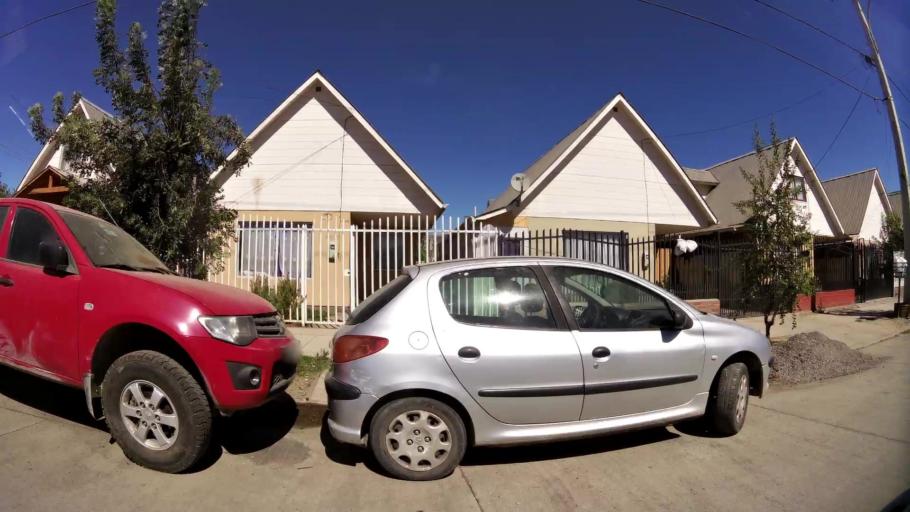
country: CL
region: O'Higgins
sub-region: Provincia de Cachapoal
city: Rancagua
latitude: -34.1778
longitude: -70.7780
